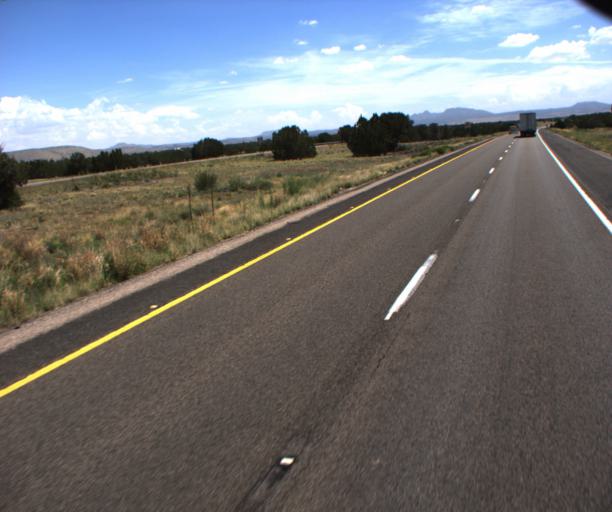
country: US
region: Arizona
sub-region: Mohave County
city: Peach Springs
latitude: 35.3200
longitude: -112.9465
